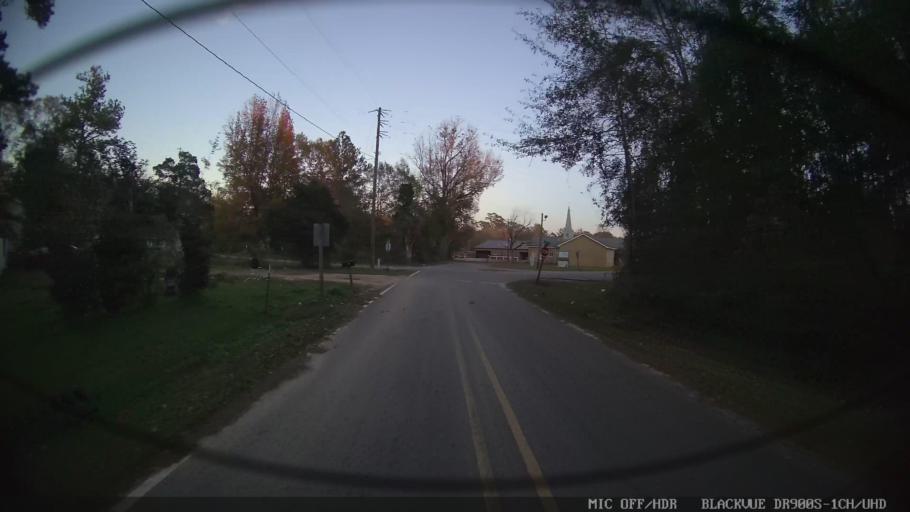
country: US
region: Mississippi
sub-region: Stone County
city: Wiggins
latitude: 31.0581
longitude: -89.1870
